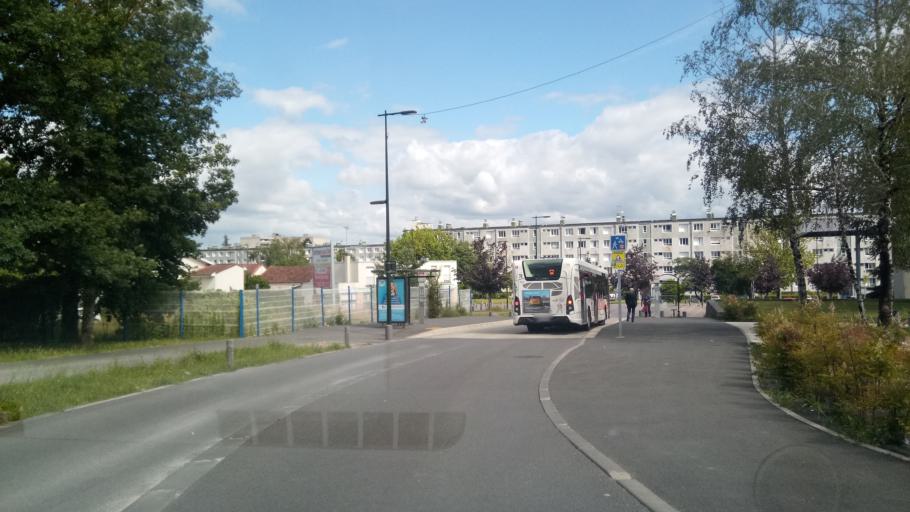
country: FR
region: Poitou-Charentes
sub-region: Departement de la Charente
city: Angouleme
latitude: 45.6484
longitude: 0.1256
